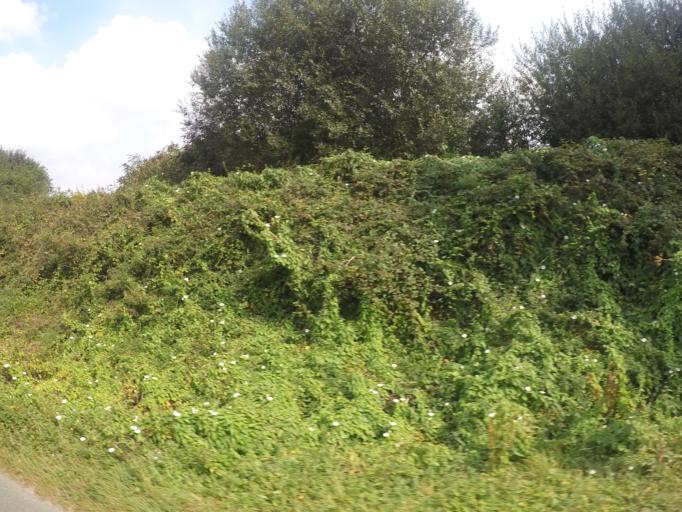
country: FR
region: Brittany
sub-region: Departement des Cotes-d'Armor
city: Plelo
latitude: 48.5444
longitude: -2.9455
